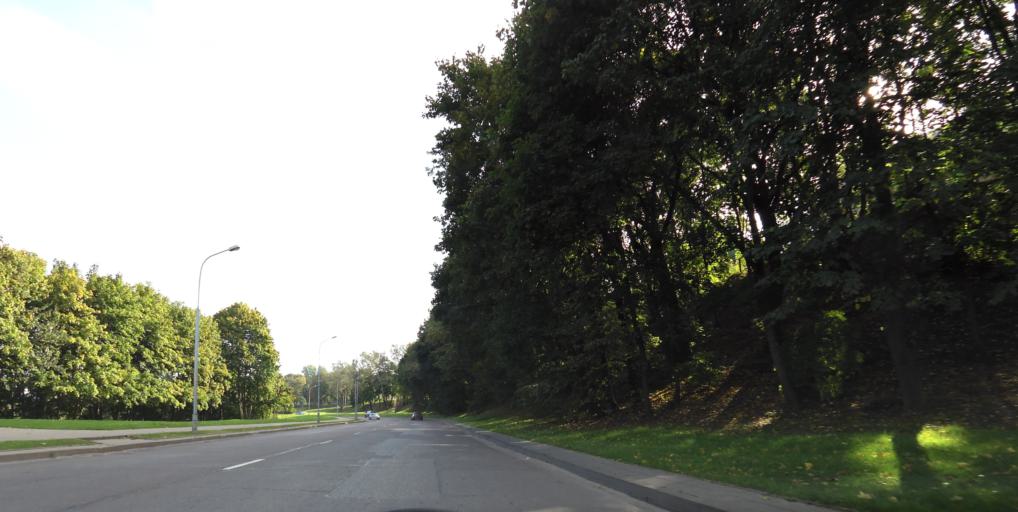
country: LT
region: Vilnius County
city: Rasos
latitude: 54.6778
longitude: 25.2962
